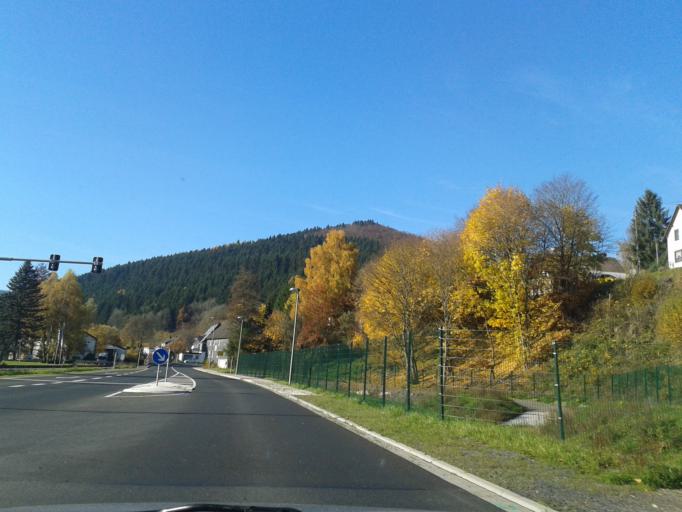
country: DE
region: North Rhine-Westphalia
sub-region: Regierungsbezirk Arnsberg
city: Bad Laasphe
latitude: 50.9491
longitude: 8.3728
